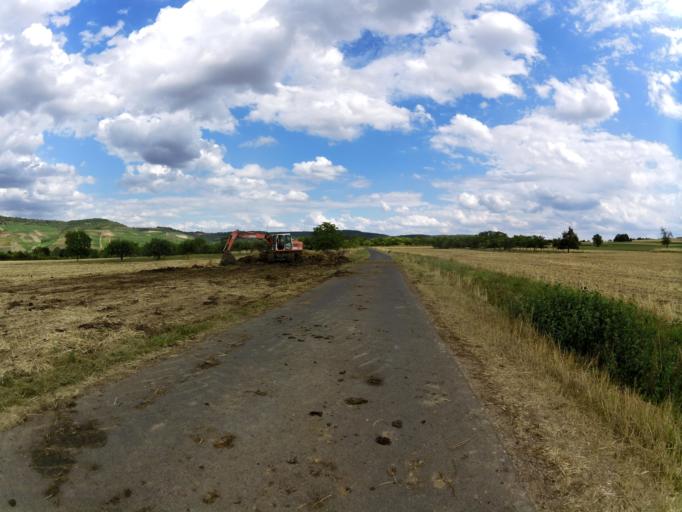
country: DE
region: Bavaria
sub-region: Regierungsbezirk Unterfranken
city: Zellingen
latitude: 49.8821
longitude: 9.8242
